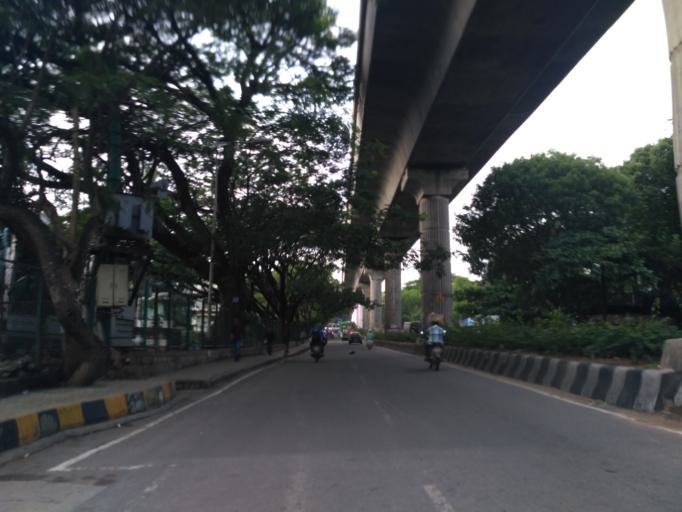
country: IN
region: Karnataka
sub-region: Bangalore Urban
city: Bangalore
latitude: 12.9628
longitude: 77.5339
